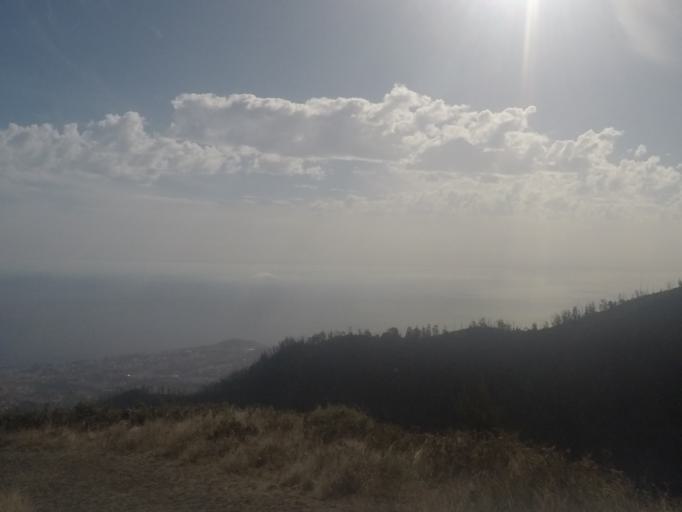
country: PT
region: Madeira
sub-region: Funchal
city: Nossa Senhora do Monte
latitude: 32.7022
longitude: -16.9168
